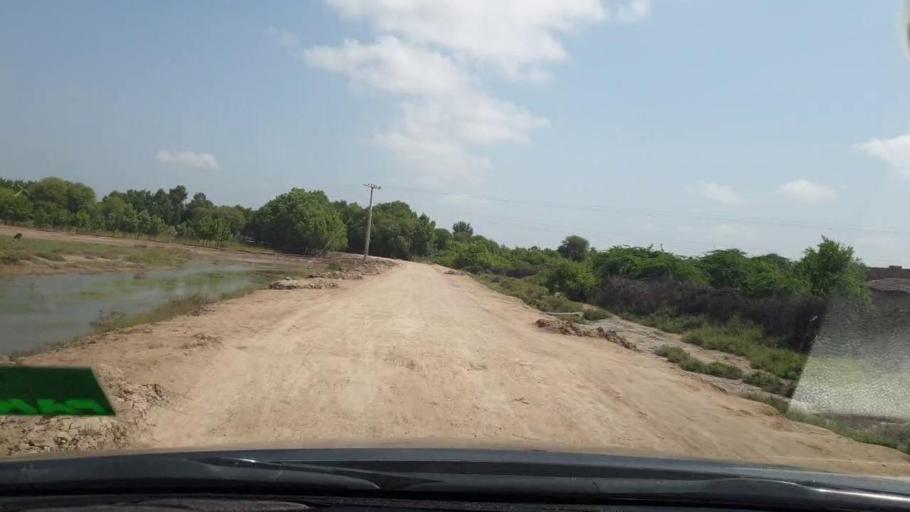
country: PK
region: Sindh
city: Tando Bago
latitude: 24.9493
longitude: 69.0757
